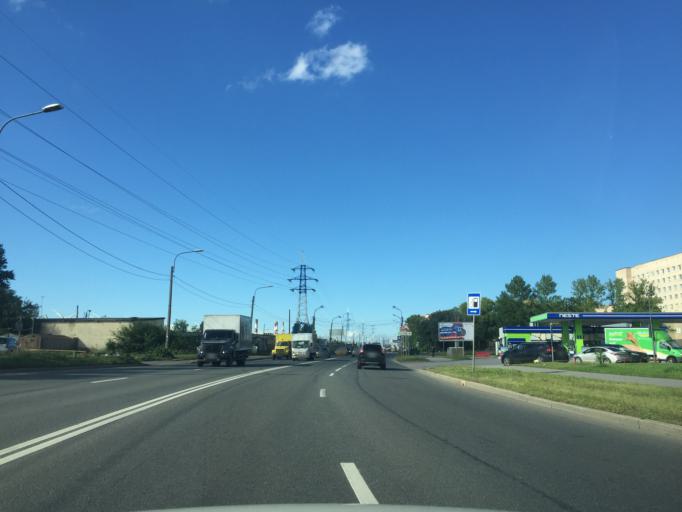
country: RU
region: St.-Petersburg
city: Avtovo
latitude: 59.8470
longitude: 30.2919
